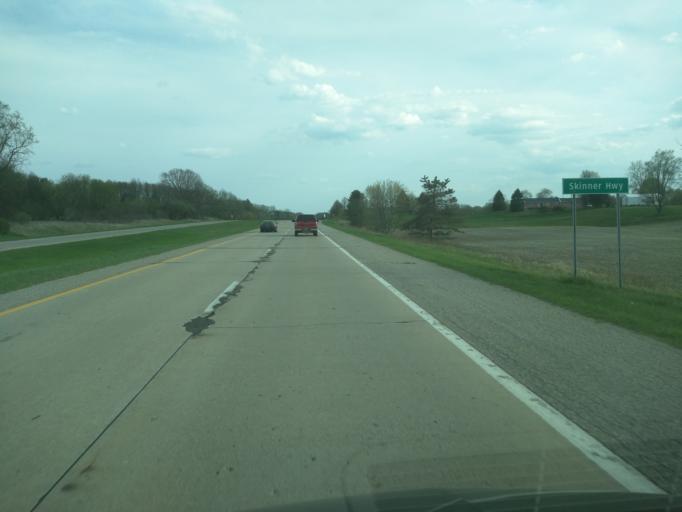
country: US
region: Michigan
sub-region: Eaton County
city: Dimondale
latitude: 42.6242
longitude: -84.6229
